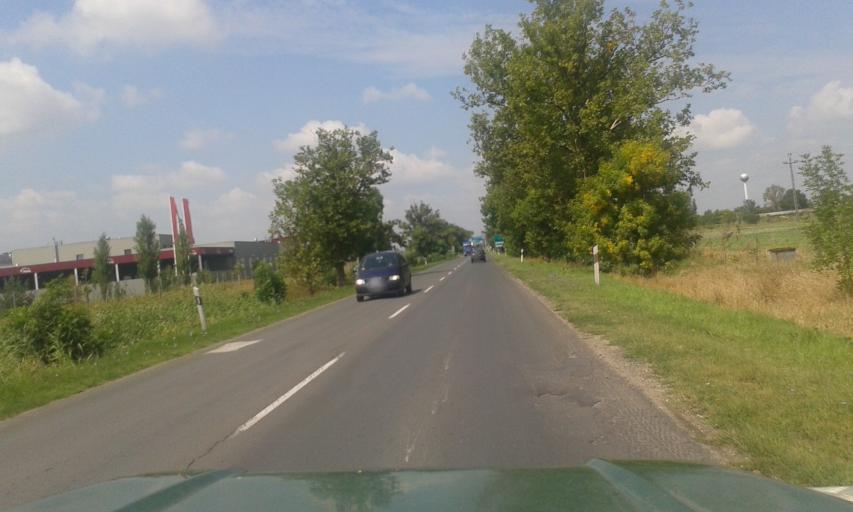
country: HU
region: Csongrad
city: Szeged
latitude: 46.2861
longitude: 20.0891
